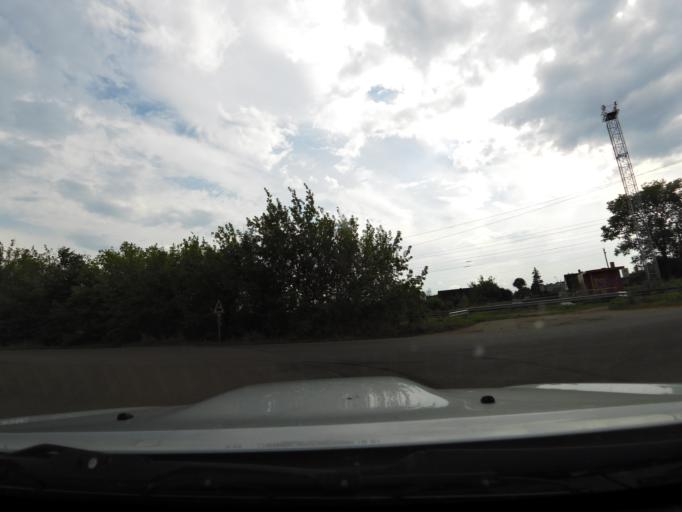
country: LT
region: Vilnius County
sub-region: Vilniaus Rajonas
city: Vievis
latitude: 54.7753
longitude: 24.8223
